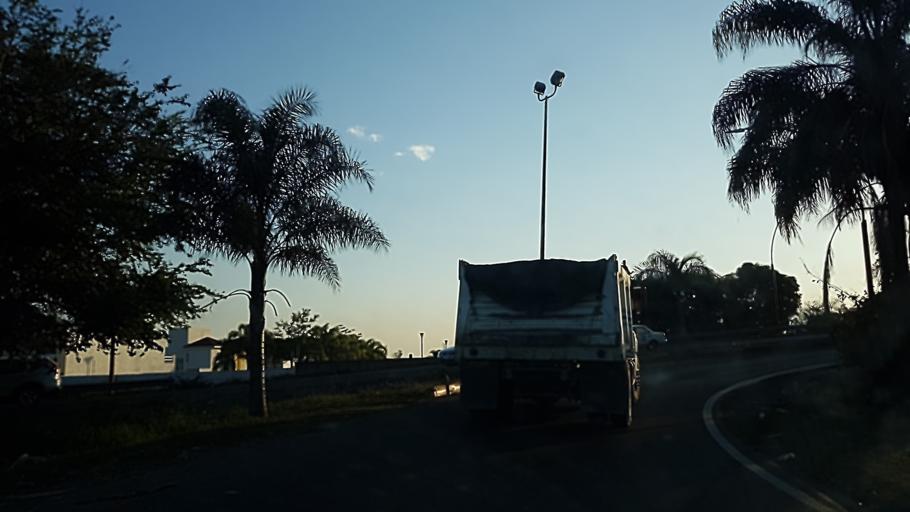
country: MX
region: Nayarit
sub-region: Tepic
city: La Corregidora
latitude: 21.4687
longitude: -104.8447
